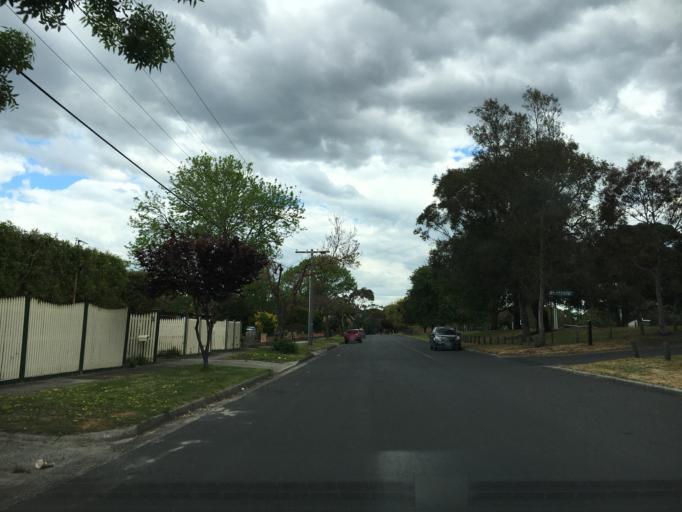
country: AU
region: Victoria
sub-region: Monash
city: Oakleigh South
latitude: -37.9111
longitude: 145.0941
